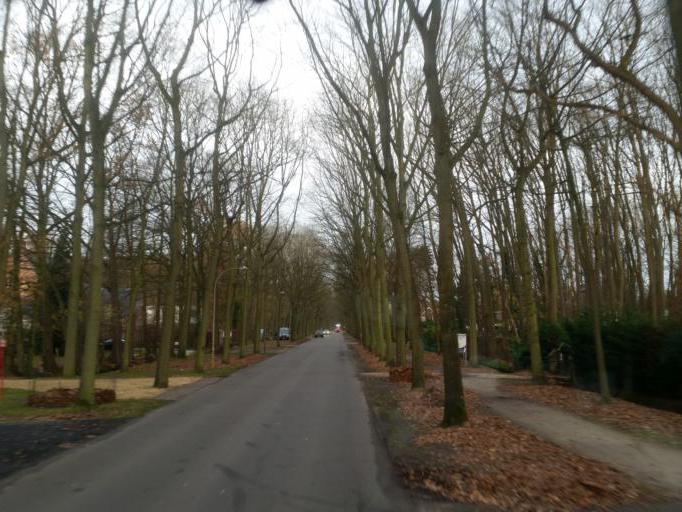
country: BE
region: Flanders
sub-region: Provincie Antwerpen
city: Brasschaat
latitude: 51.3114
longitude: 4.5036
